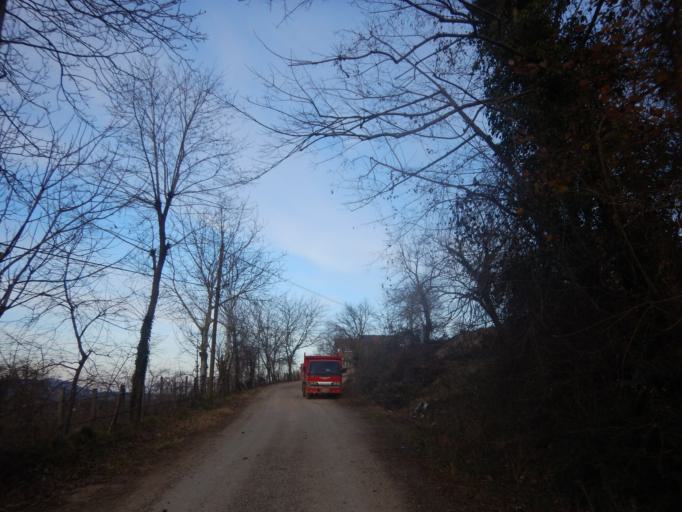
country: TR
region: Ordu
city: Uzunisa
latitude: 40.9024
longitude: 37.8275
